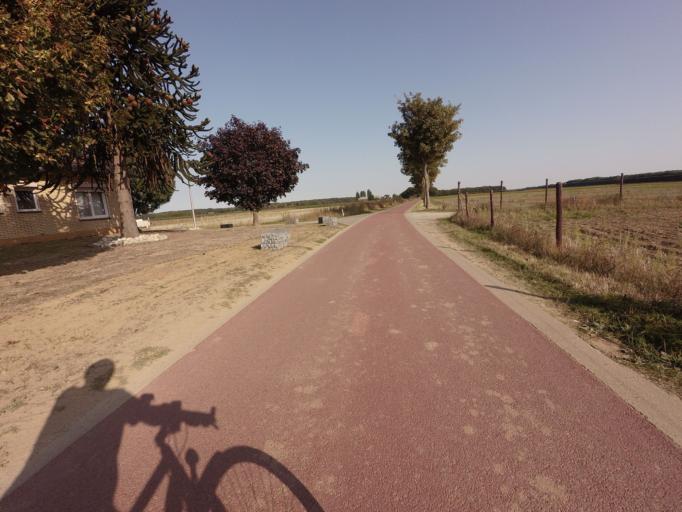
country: NL
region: Limburg
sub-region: Gemeente Roerdalen
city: Montfort
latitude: 51.1522
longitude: 5.9529
